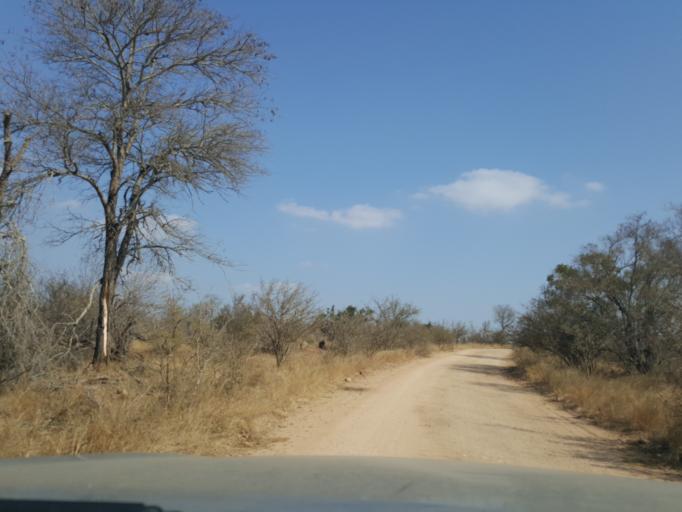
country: ZA
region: Mpumalanga
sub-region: Ehlanzeni District
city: Komatipoort
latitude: -25.3015
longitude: 31.7562
